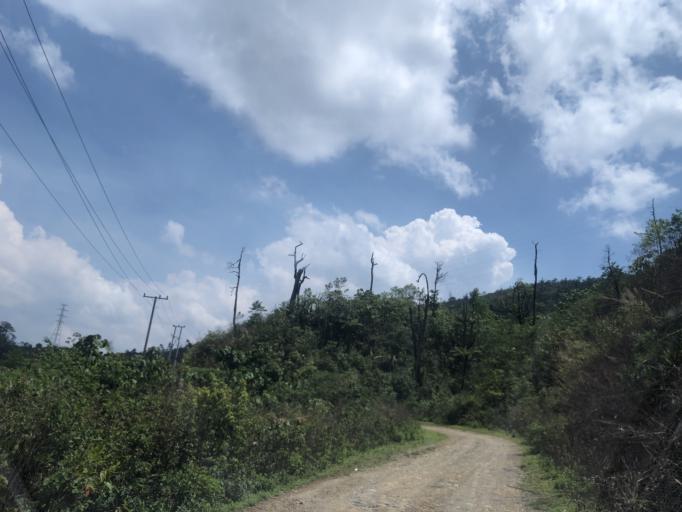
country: LA
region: Phongsali
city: Phongsali
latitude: 21.3939
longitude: 102.1922
